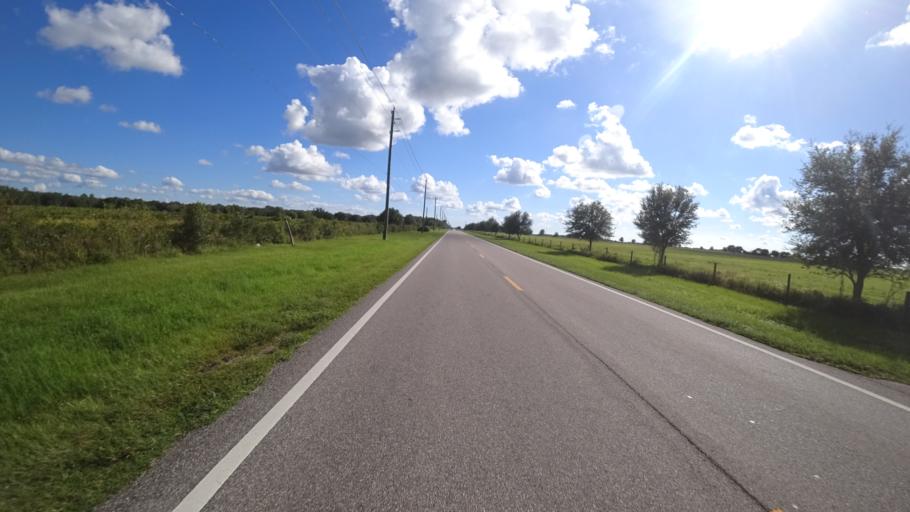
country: US
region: Florida
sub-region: Sarasota County
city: Lake Sarasota
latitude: 27.3750
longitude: -82.2683
